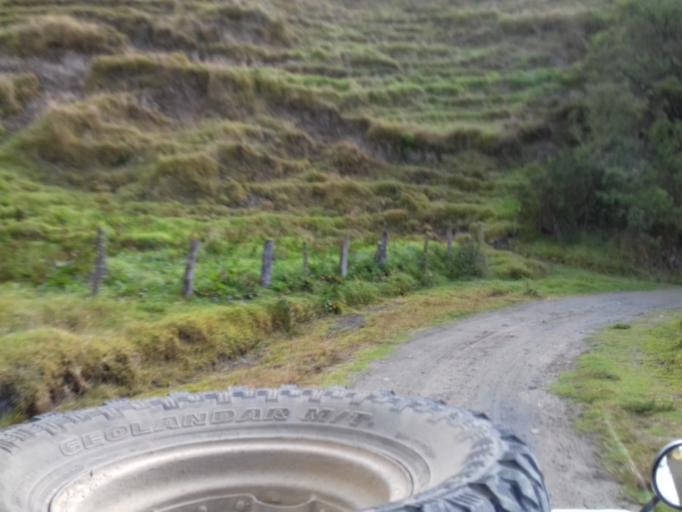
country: CO
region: Quindio
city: Salento
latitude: 4.5474
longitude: -75.4909
